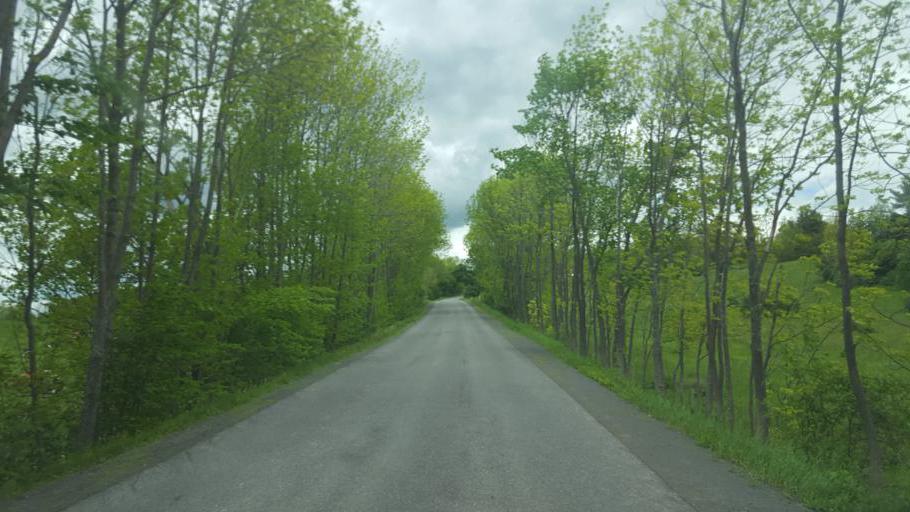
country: US
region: New York
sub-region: Otsego County
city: Richfield Springs
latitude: 42.8705
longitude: -75.0591
